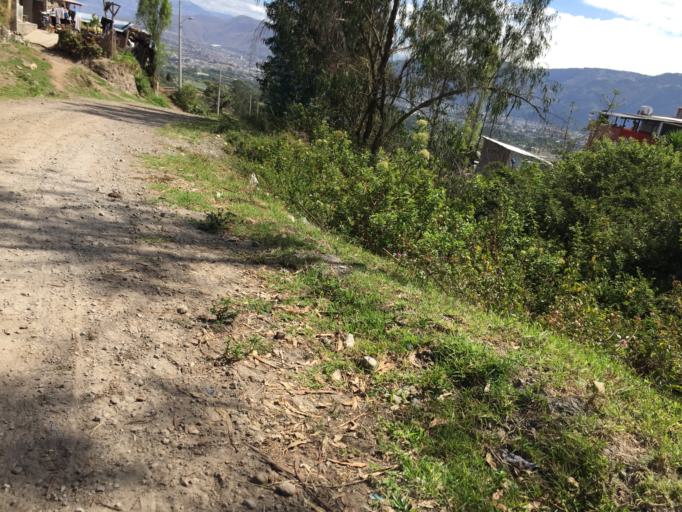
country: EC
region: Imbabura
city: Ibarra
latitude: 0.3087
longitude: -78.1587
